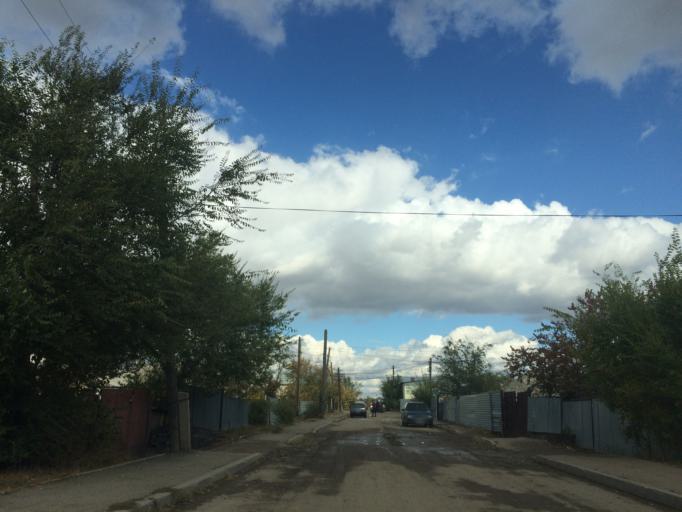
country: KZ
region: Astana Qalasy
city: Astana
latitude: 51.1852
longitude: 71.3835
